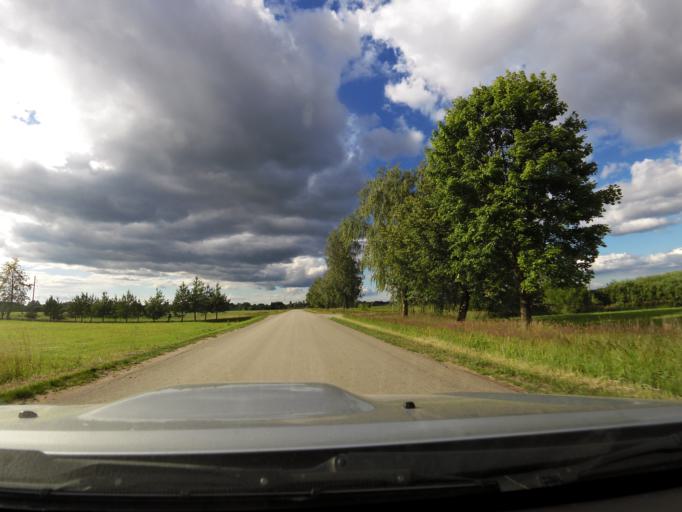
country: LT
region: Panevezys
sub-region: Birzai
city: Birzai
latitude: 56.3838
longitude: 24.7730
